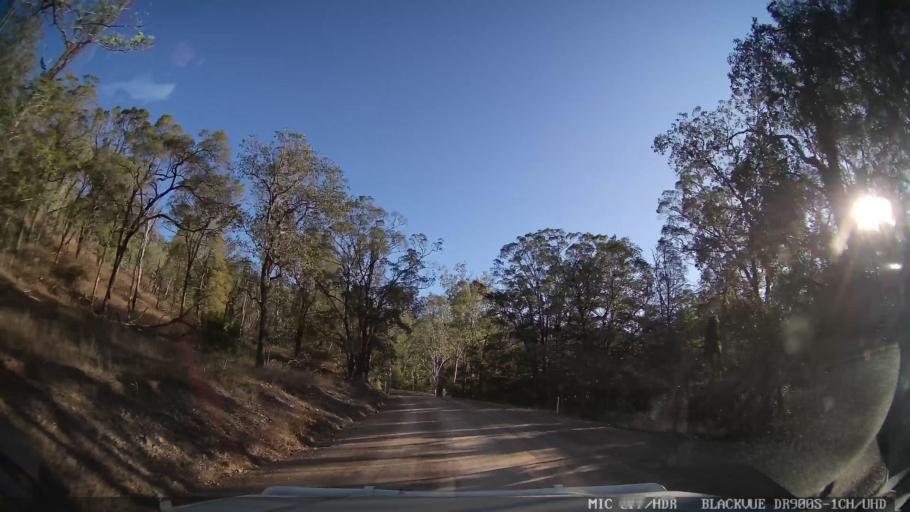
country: AU
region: Queensland
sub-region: Gladstone
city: Toolooa
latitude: -24.6953
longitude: 151.4052
